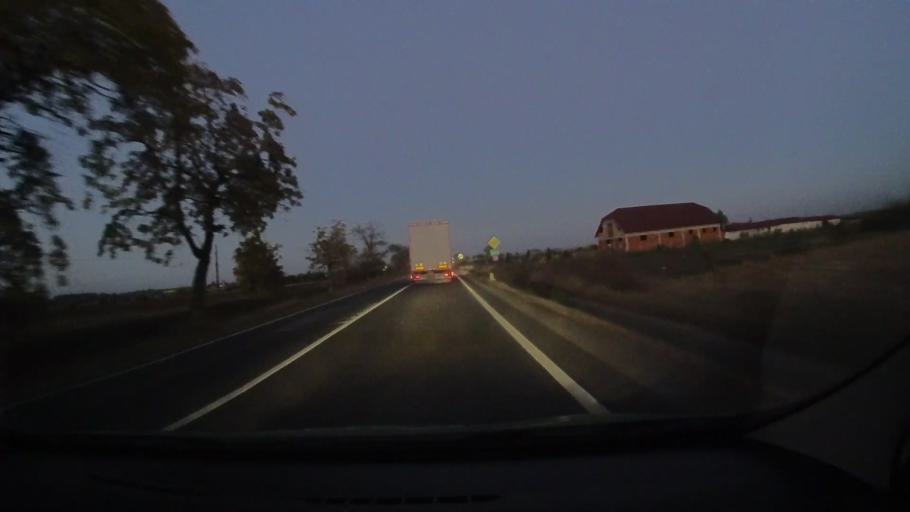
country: RO
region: Bihor
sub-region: Comuna Valea lui Mihai
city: Valea lui Mihai
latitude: 47.5157
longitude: 22.1567
